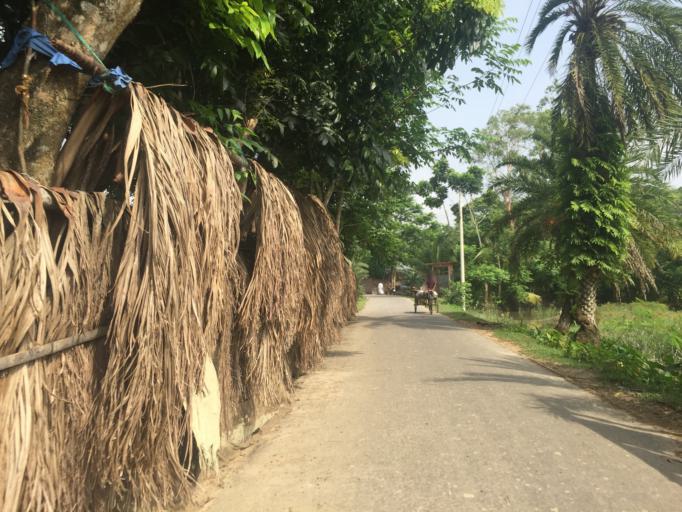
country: BD
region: Barisal
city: Mathba
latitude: 22.2136
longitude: 89.9210
